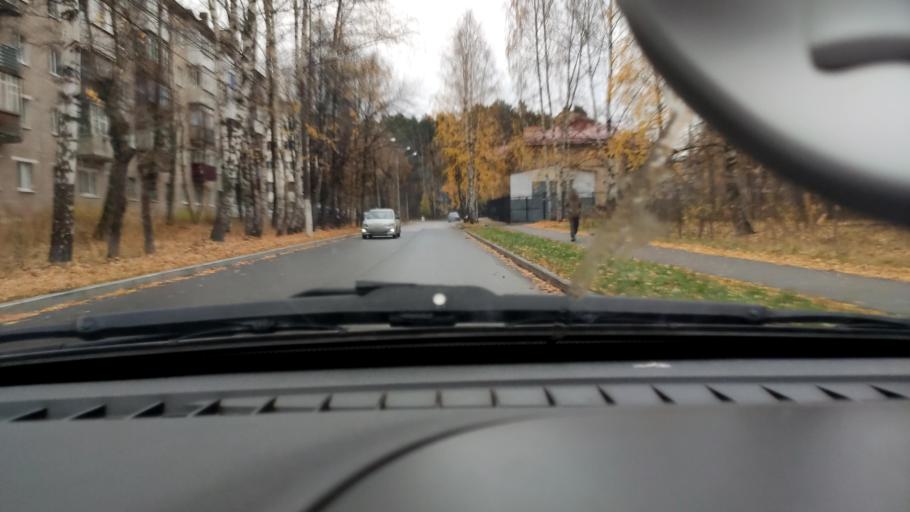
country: RU
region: Perm
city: Kultayevo
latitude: 58.0119
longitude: 55.9663
